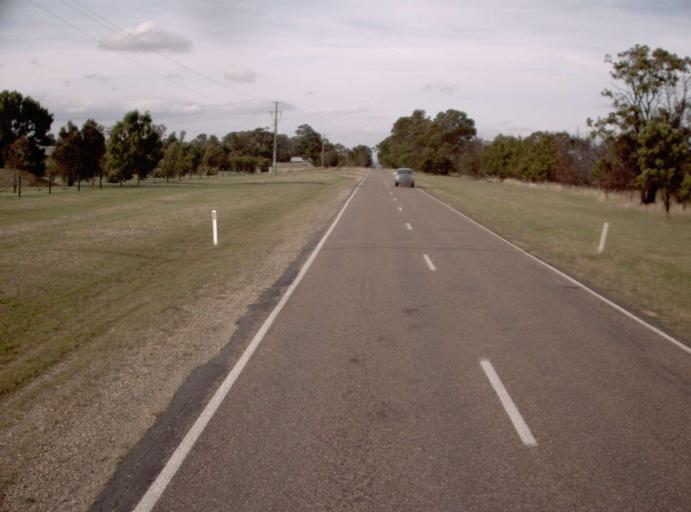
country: AU
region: Victoria
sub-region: Wellington
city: Heyfield
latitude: -38.0364
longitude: 146.6667
